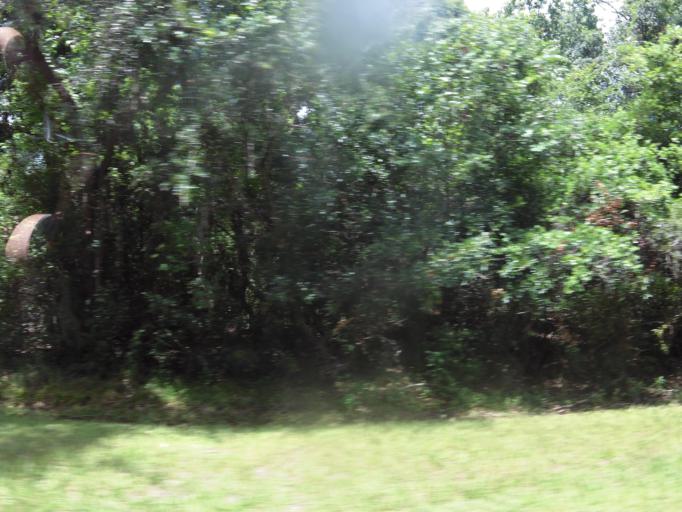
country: US
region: Georgia
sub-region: Camden County
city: St. Marys
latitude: 30.7326
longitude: -81.5497
